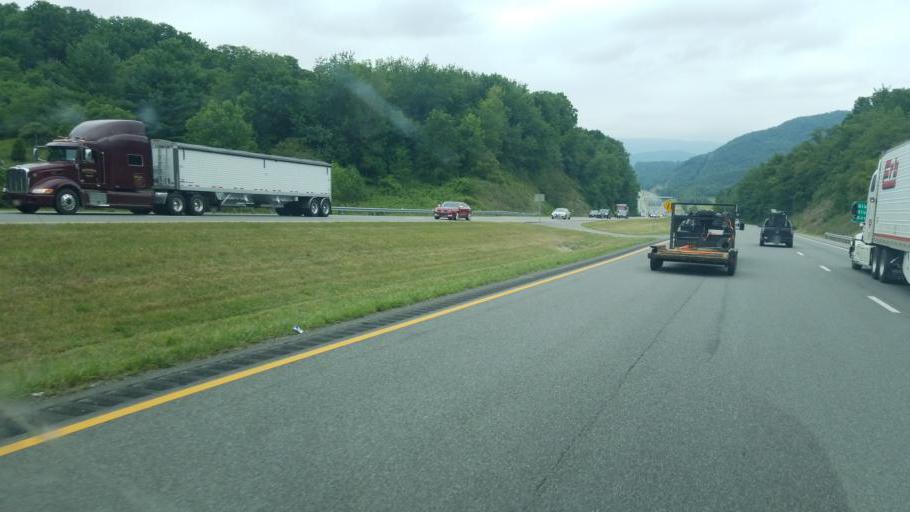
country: US
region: Virginia
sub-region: Wythe County
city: Wytheville
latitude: 36.9756
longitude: -81.0685
